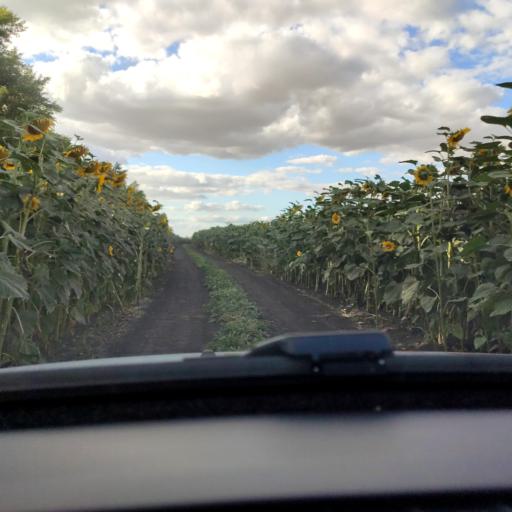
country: RU
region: Voronezj
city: Verkhnyaya Khava
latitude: 51.5963
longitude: 39.8414
